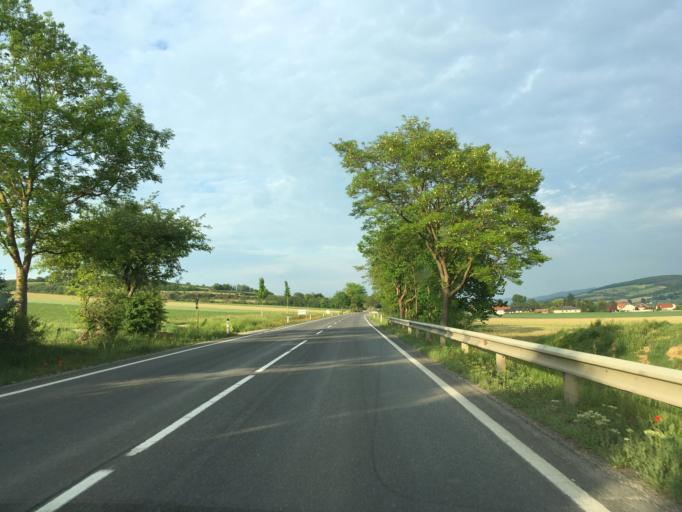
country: AT
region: Lower Austria
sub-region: Politischer Bezirk Tulln
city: Michelhausen
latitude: 48.2710
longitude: 15.9740
